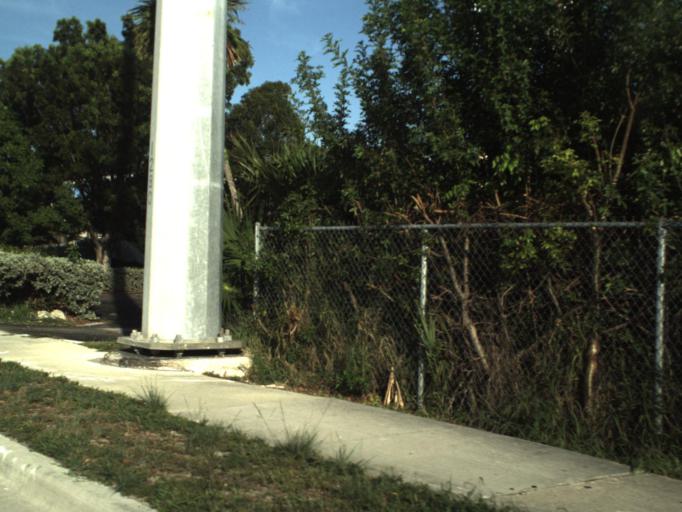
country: US
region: Florida
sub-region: Monroe County
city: Marathon
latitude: 24.7333
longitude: -81.0170
